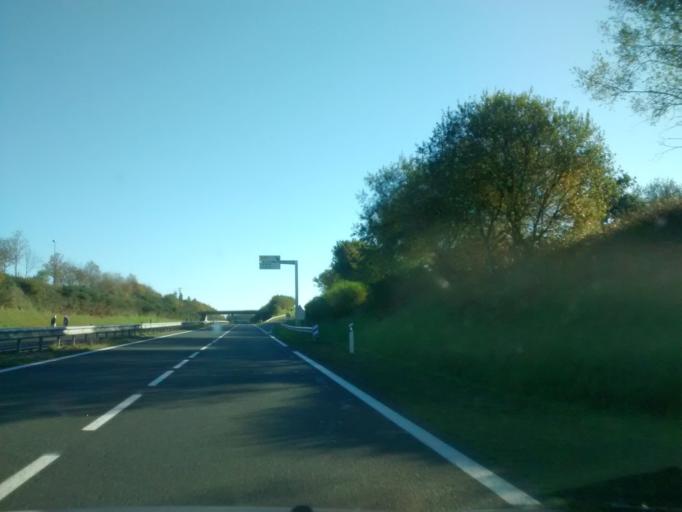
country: FR
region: Brittany
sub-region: Departement des Cotes-d'Armor
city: Cavan
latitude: 48.6774
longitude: -3.3546
